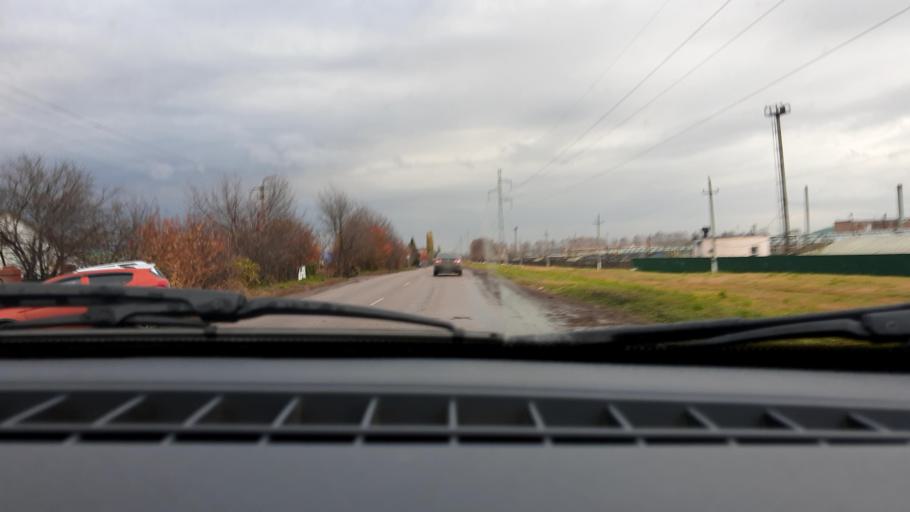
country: RU
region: Bashkortostan
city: Ufa
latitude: 54.8405
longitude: 55.9985
